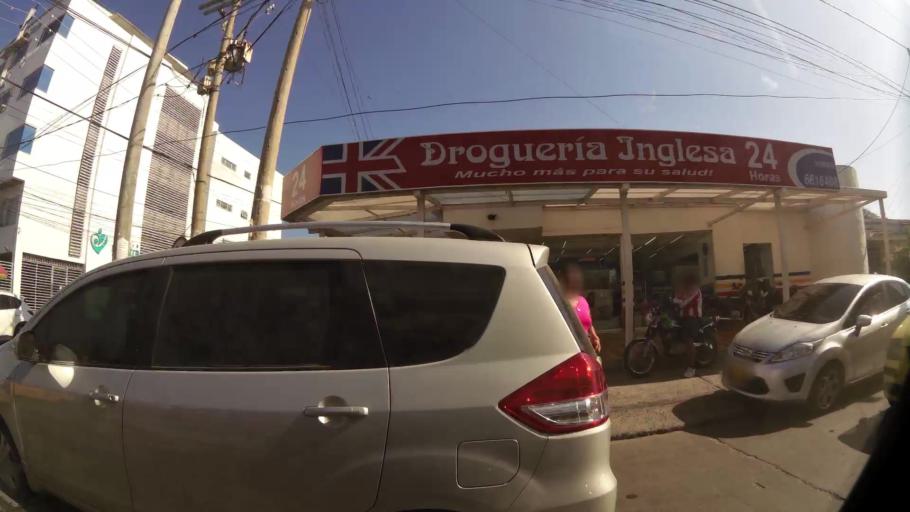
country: CO
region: Bolivar
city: Cartagena
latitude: 10.3916
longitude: -75.4790
